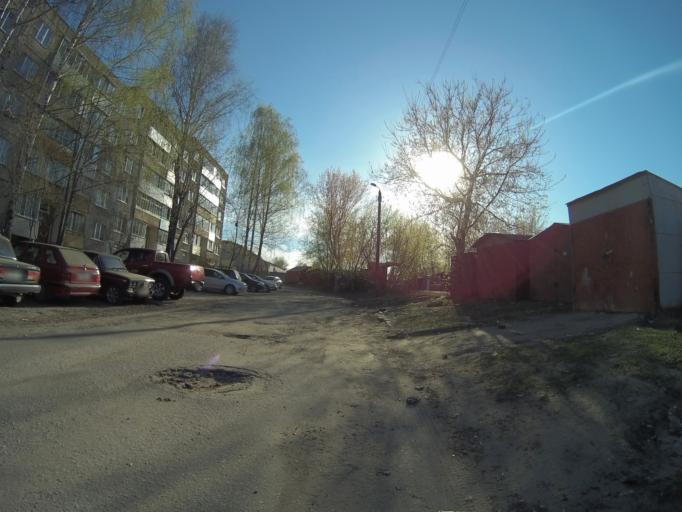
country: RU
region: Vladimir
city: Vladimir
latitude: 56.1496
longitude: 40.4121
